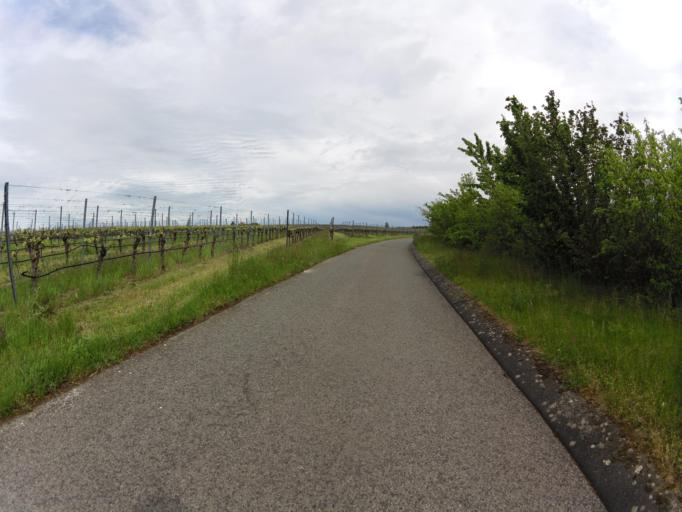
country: DE
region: Bavaria
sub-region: Regierungsbezirk Unterfranken
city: Nordheim
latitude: 49.8501
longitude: 10.1794
